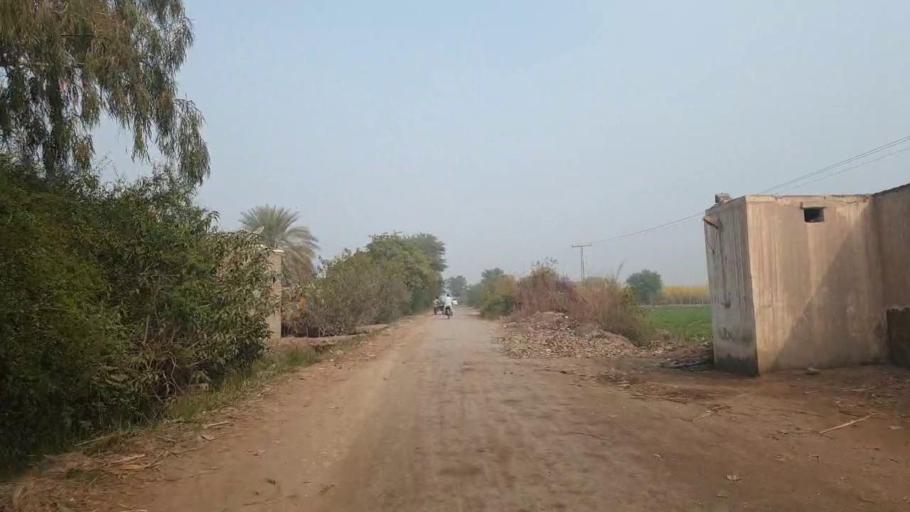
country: PK
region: Sindh
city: Tando Adam
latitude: 25.7901
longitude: 68.6103
